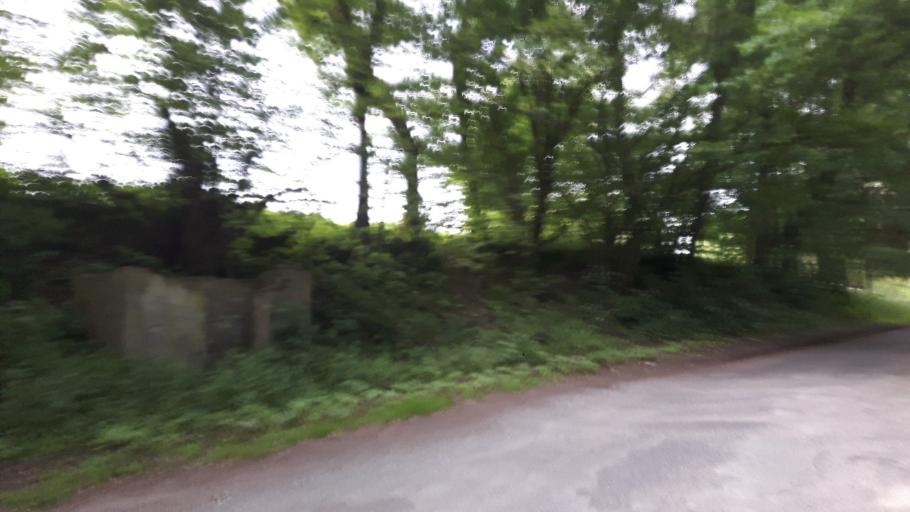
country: PL
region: West Pomeranian Voivodeship
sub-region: Powiat gryficki
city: Gryfice
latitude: 53.8335
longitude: 15.1459
